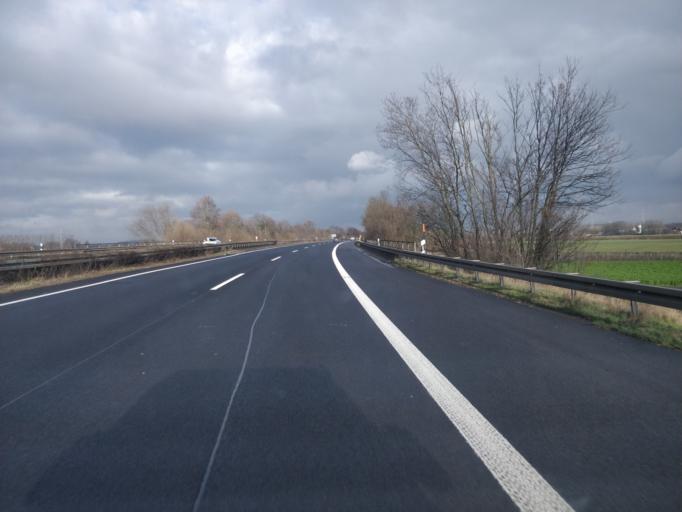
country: DE
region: North Rhine-Westphalia
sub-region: Regierungsbezirk Koln
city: Erftstadt
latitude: 50.8195
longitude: 6.7854
